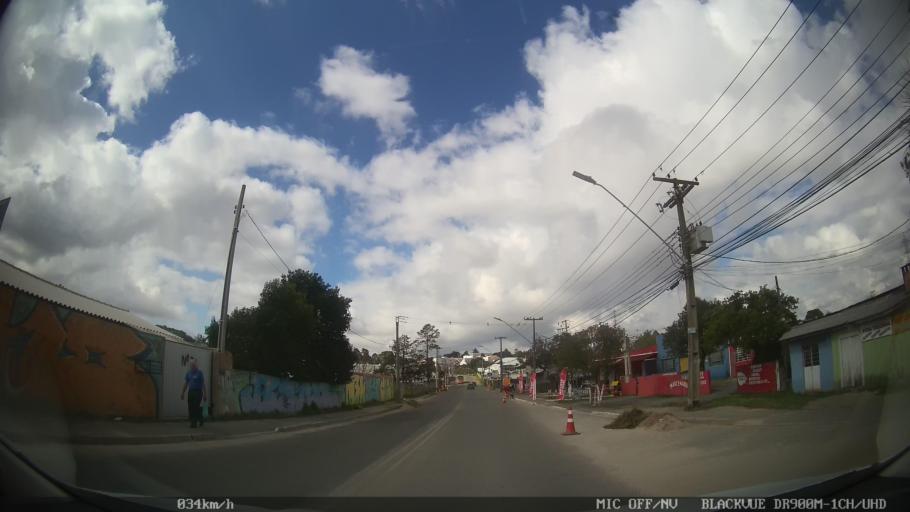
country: BR
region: Parana
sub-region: Pinhais
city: Pinhais
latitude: -25.3717
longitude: -49.2073
